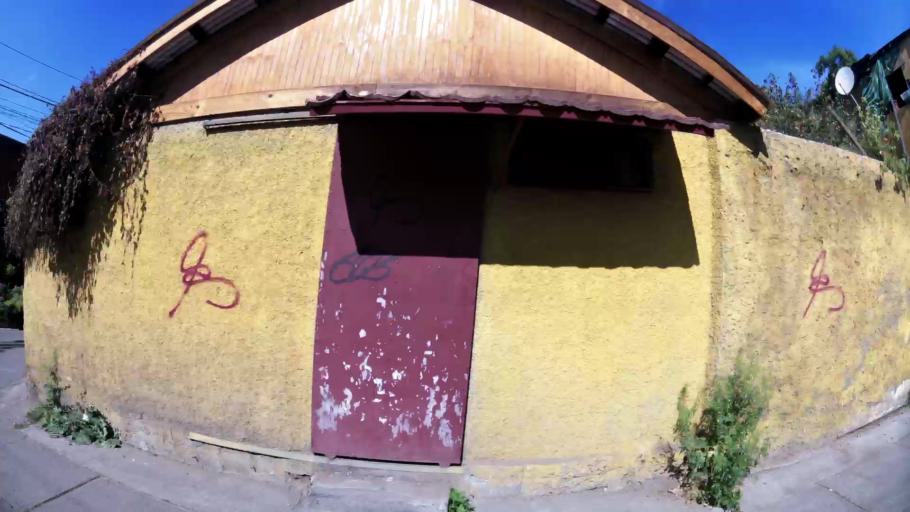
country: CL
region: Santiago Metropolitan
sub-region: Provincia de Santiago
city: Villa Presidente Frei, Nunoa, Santiago, Chile
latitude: -33.4817
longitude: -70.5721
